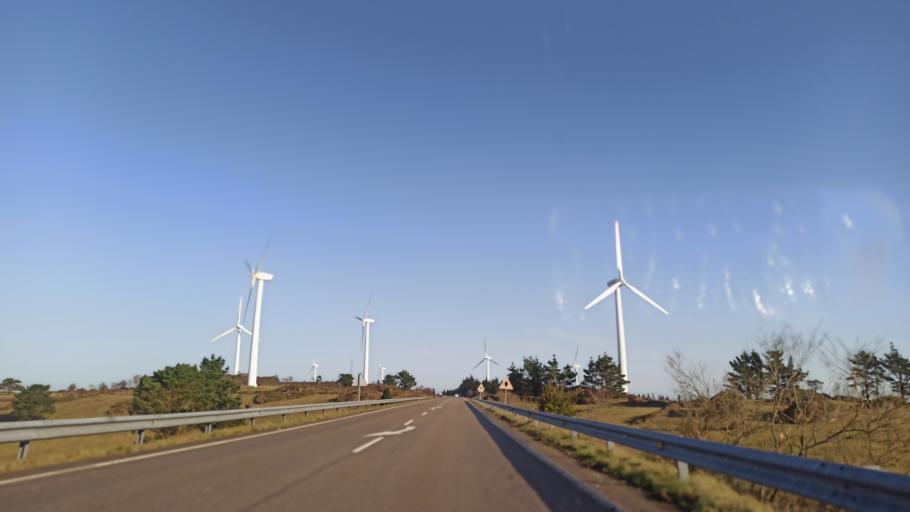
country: ES
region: Galicia
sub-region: Provincia da Coruna
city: As Pontes de Garcia Rodriguez
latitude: 43.5363
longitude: -7.8072
